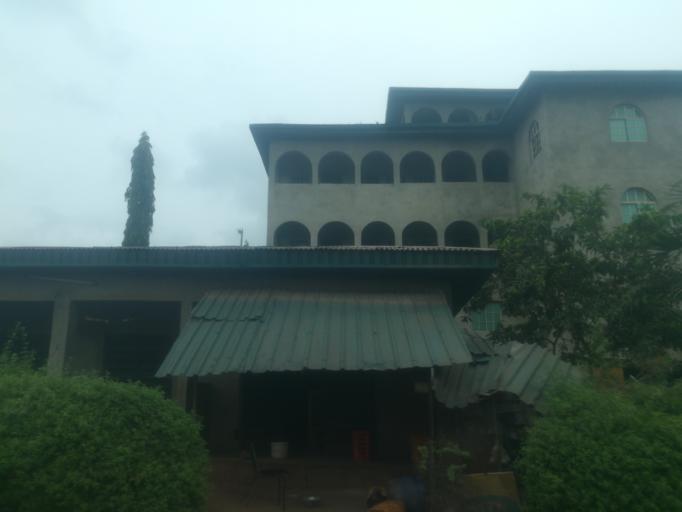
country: NG
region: Ogun
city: Itori
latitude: 7.1023
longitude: 3.1685
